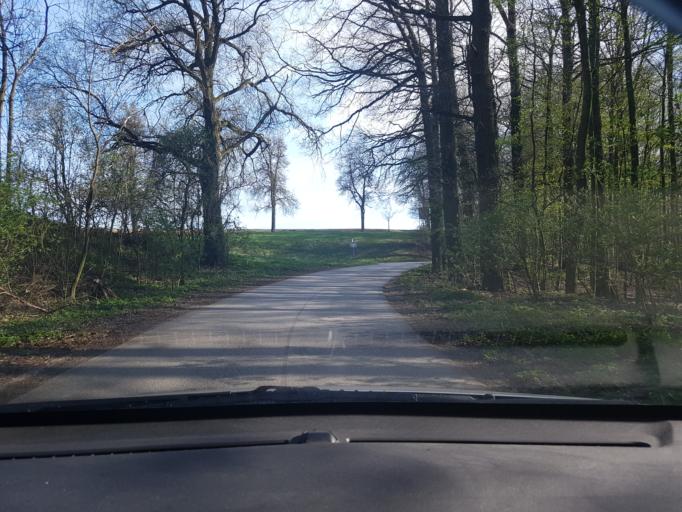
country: AT
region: Upper Austria
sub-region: Politischer Bezirk Linz-Land
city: Ansfelden
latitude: 48.1749
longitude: 14.3299
